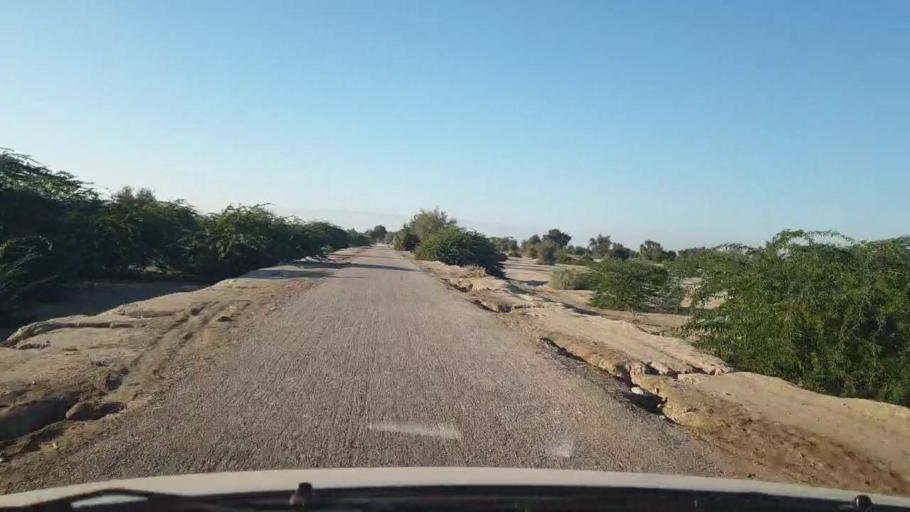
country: PK
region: Sindh
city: Johi
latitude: 26.7729
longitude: 67.4559
